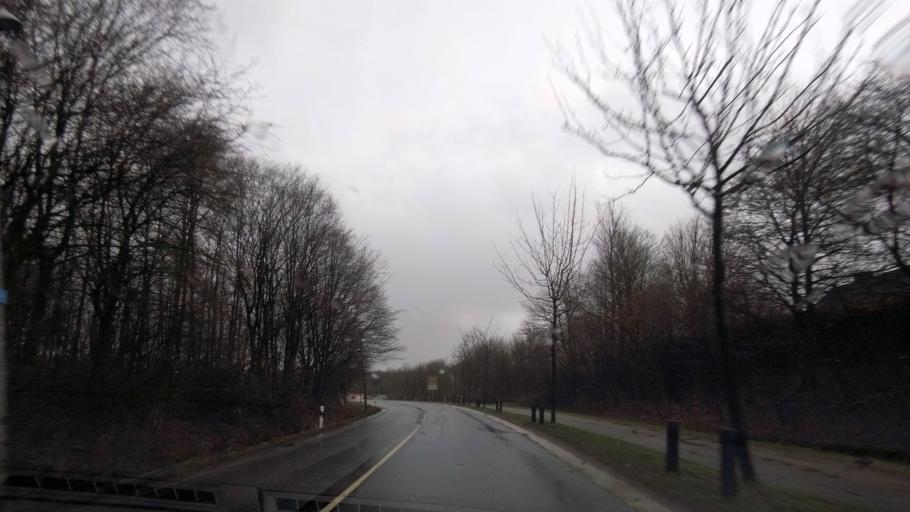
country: DE
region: Schleswig-Holstein
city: Harrislee
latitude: 54.7967
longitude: 9.4116
